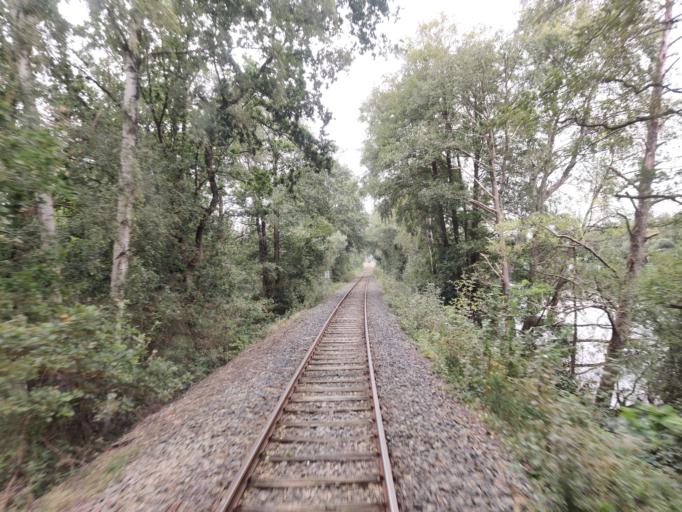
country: DE
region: Lower Saxony
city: Gnarrenburg
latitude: 53.4081
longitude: 9.0104
